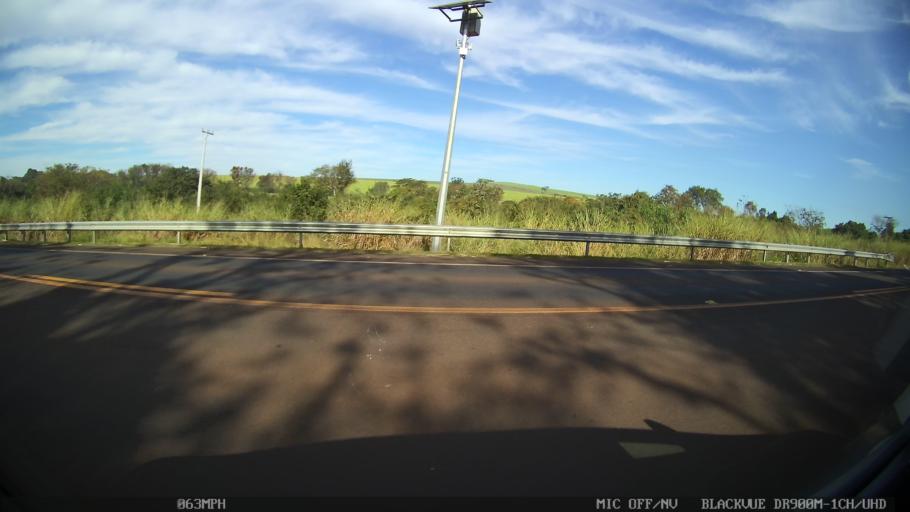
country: BR
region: Sao Paulo
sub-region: Americo Brasiliense
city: Americo Brasiliense
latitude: -21.7594
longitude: -48.0749
